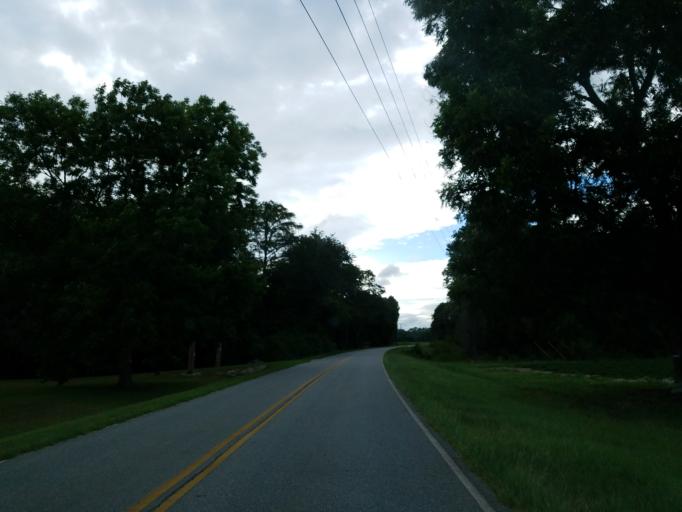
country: US
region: Georgia
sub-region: Cook County
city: Sparks
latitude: 31.2164
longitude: -83.4667
